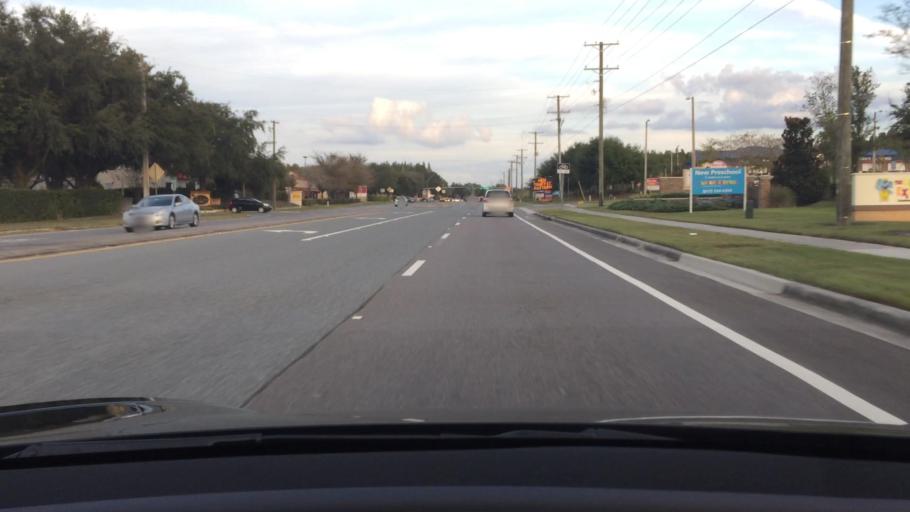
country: US
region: Florida
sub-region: Hillsborough County
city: Pebble Creek
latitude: 28.1712
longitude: -82.3579
